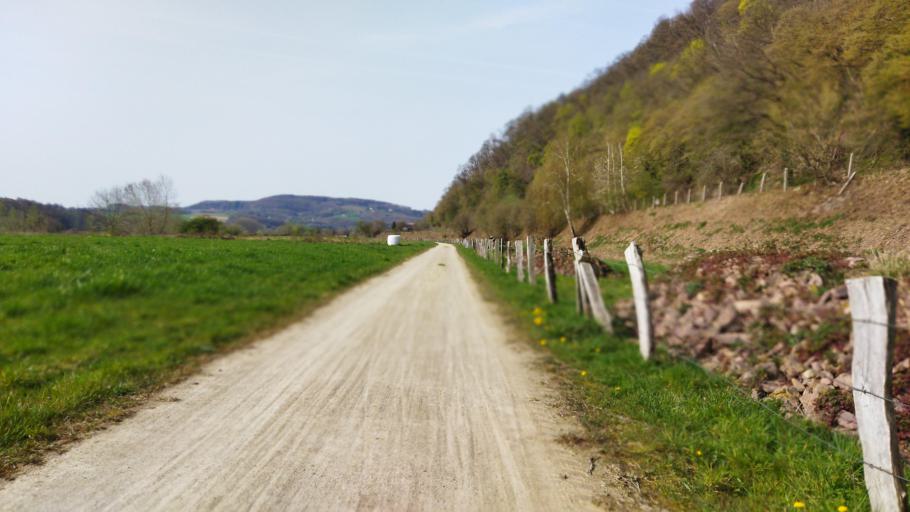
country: DE
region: North Rhine-Westphalia
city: Porta Westfalica
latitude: 52.1838
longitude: 8.9236
